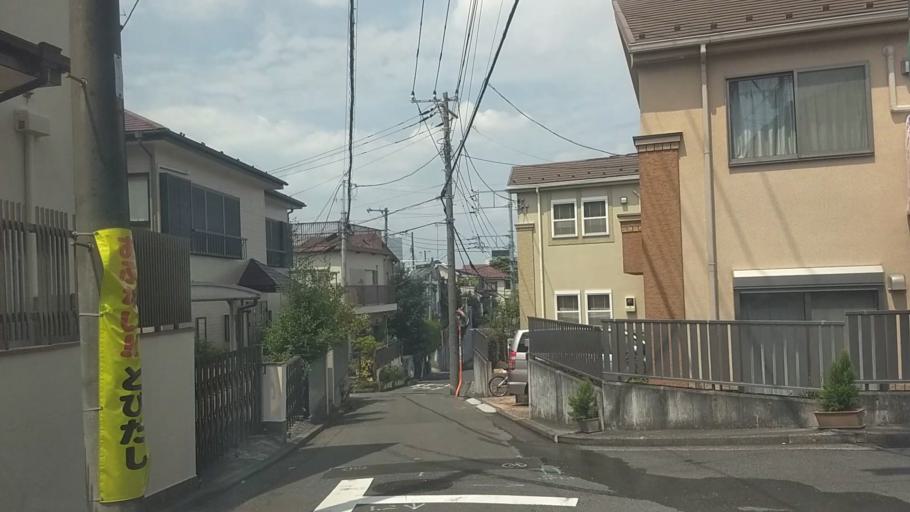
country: JP
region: Kanagawa
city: Yokohama
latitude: 35.5064
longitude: 139.6266
